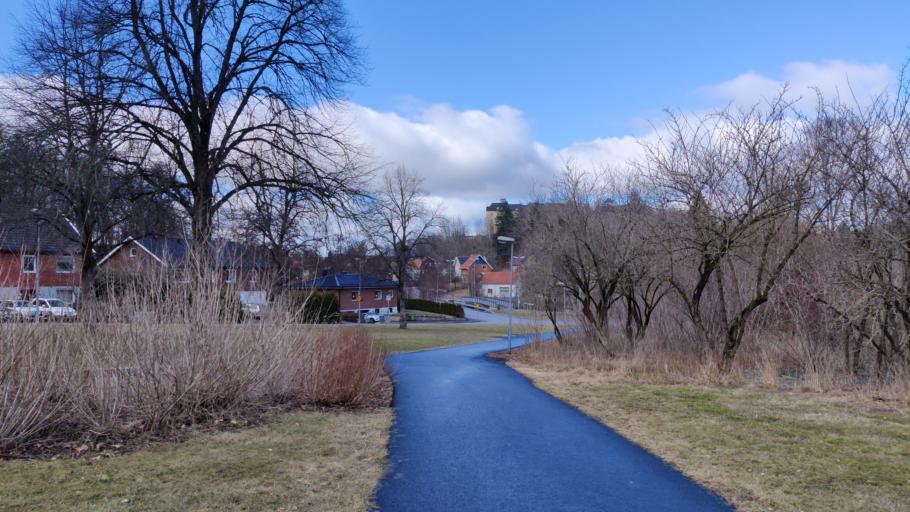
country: SE
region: Vaestra Goetaland
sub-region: Uddevalla Kommun
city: Uddevalla
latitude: 58.3437
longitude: 11.9604
